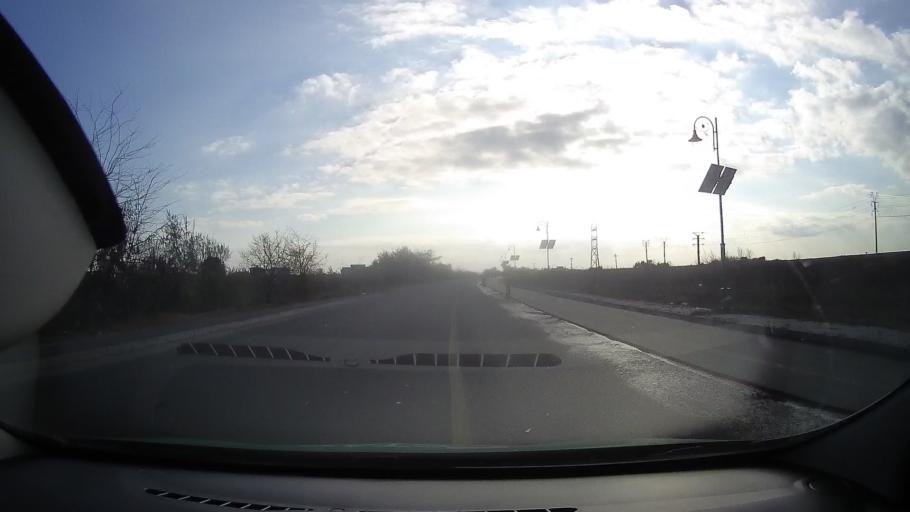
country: RO
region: Constanta
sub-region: Comuna Navodari
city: Navodari
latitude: 44.2944
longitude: 28.6129
